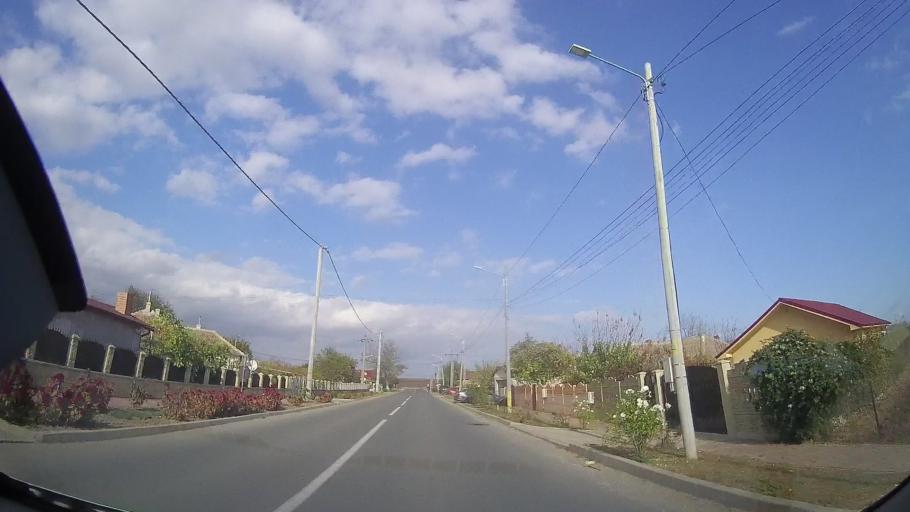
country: RO
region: Constanta
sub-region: Comuna Douazeci si Trei August
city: Dulcesti
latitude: 43.9088
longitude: 28.5494
